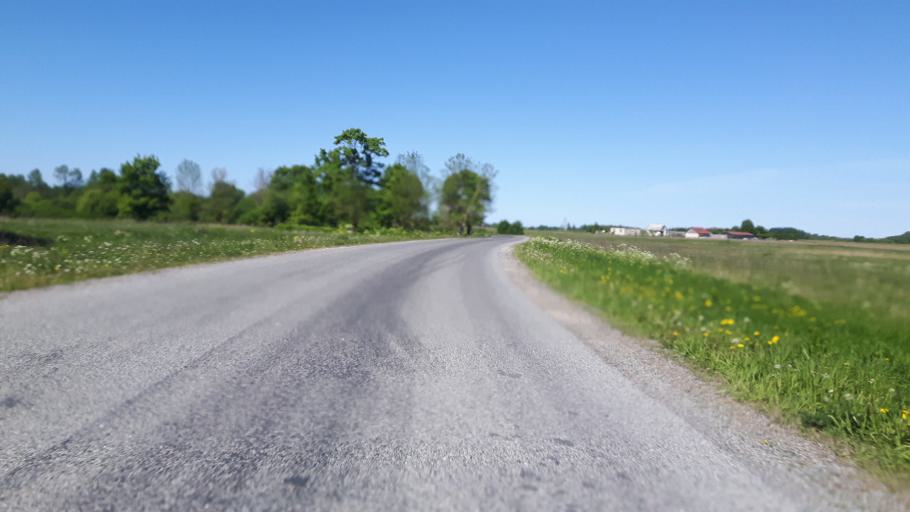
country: EE
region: Ida-Virumaa
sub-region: Sillamaee linn
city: Sillamae
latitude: 59.3790
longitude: 27.8298
